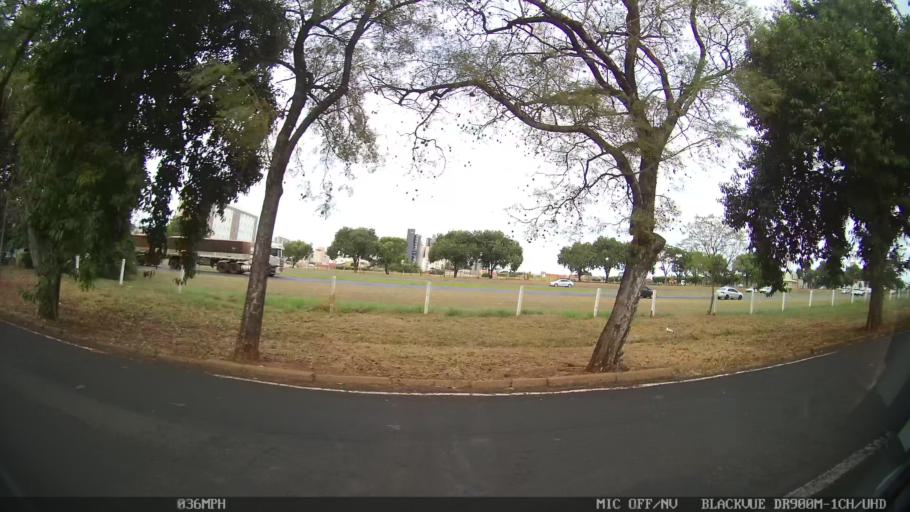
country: BR
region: Sao Paulo
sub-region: Sao Jose Do Rio Preto
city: Sao Jose do Rio Preto
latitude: -20.8246
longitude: -49.4070
